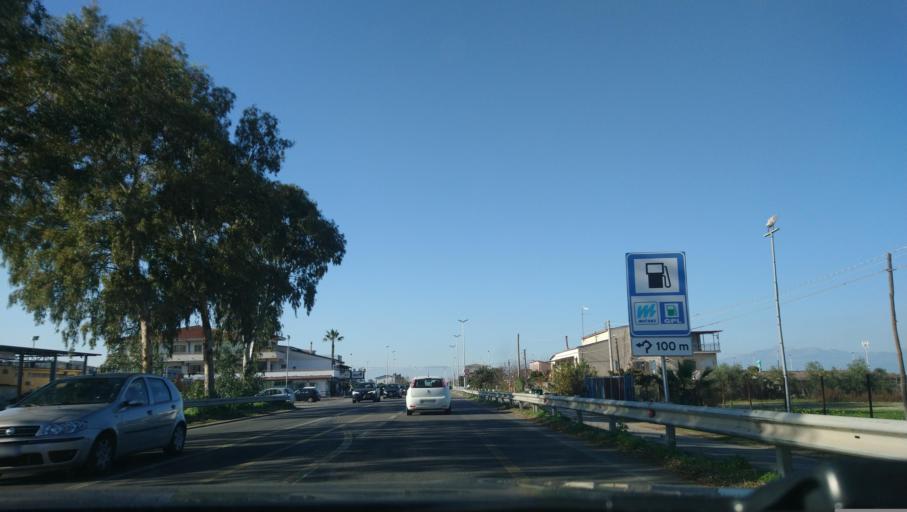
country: IT
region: Calabria
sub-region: Provincia di Cosenza
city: Fabrizio
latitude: 39.6316
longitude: 16.5670
